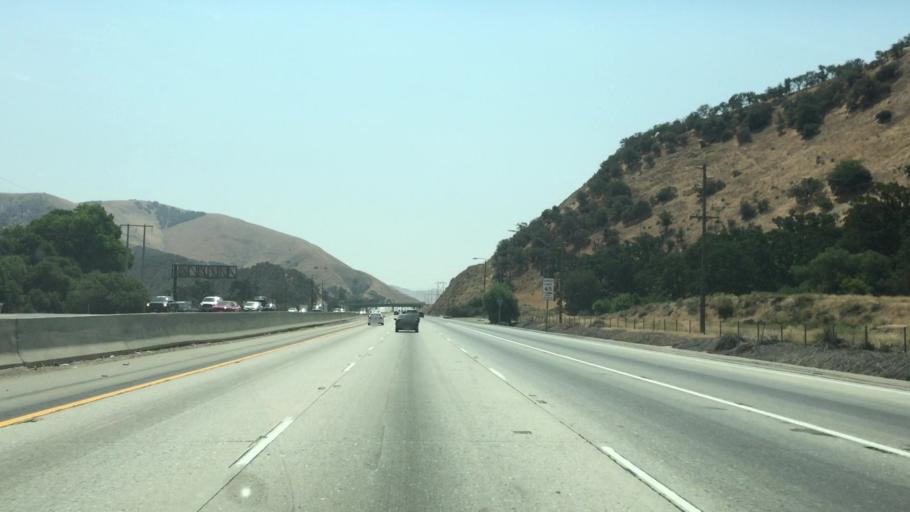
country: US
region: California
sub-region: Kern County
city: Lebec
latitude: 34.8732
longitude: -118.8908
